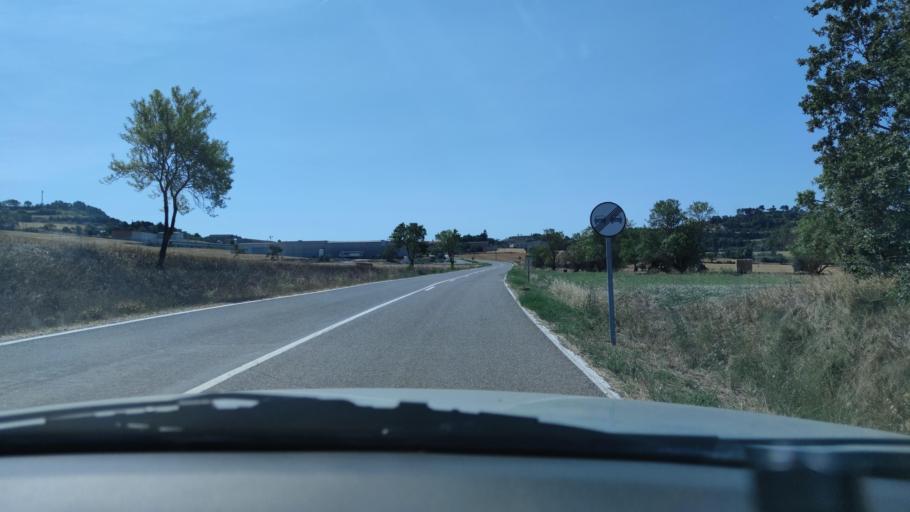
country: ES
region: Catalonia
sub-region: Provincia de Lleida
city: Sant Guim de Freixenet
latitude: 41.6235
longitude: 1.3490
